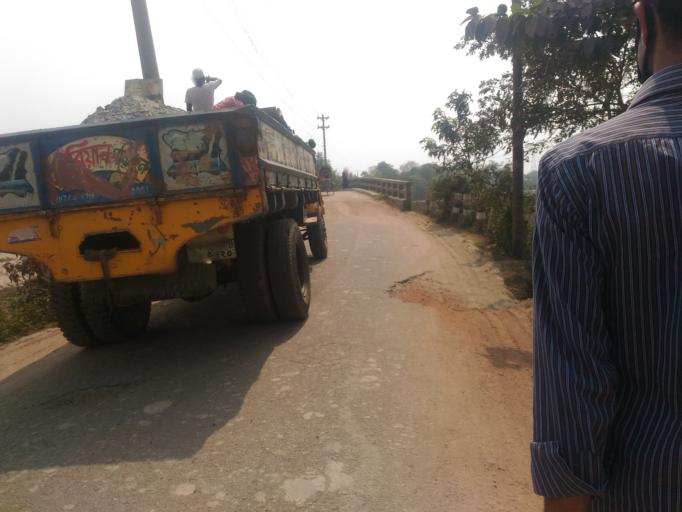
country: BD
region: Dhaka
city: Narayanganj
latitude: 23.6519
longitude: 90.4477
